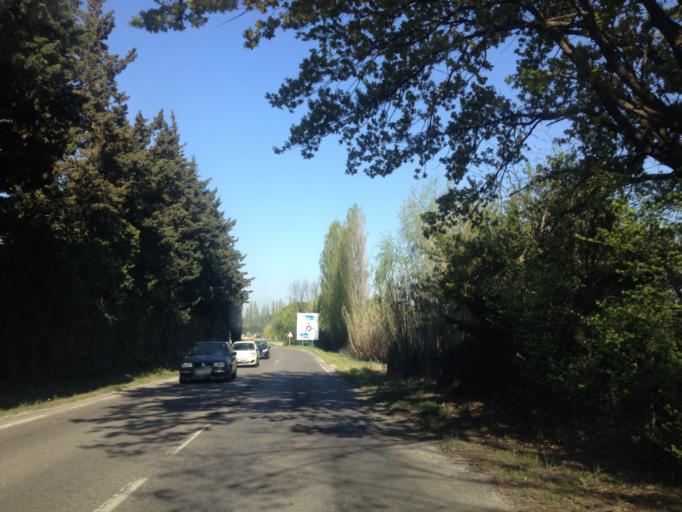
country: FR
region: Provence-Alpes-Cote d'Azur
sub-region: Departement du Vaucluse
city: Loriol-du-Comtat
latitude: 44.0724
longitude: 5.0060
